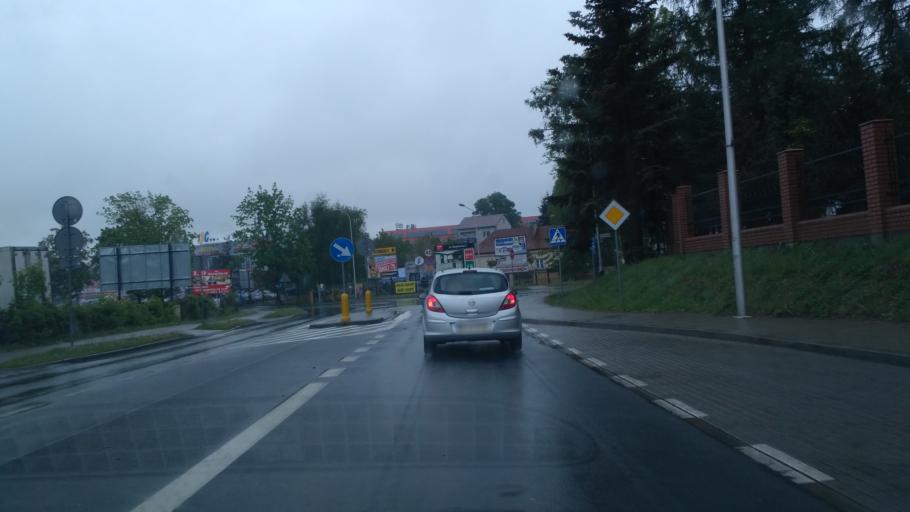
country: PL
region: Subcarpathian Voivodeship
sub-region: Powiat jaroslawski
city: Jaroslaw
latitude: 50.0102
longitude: 22.6742
